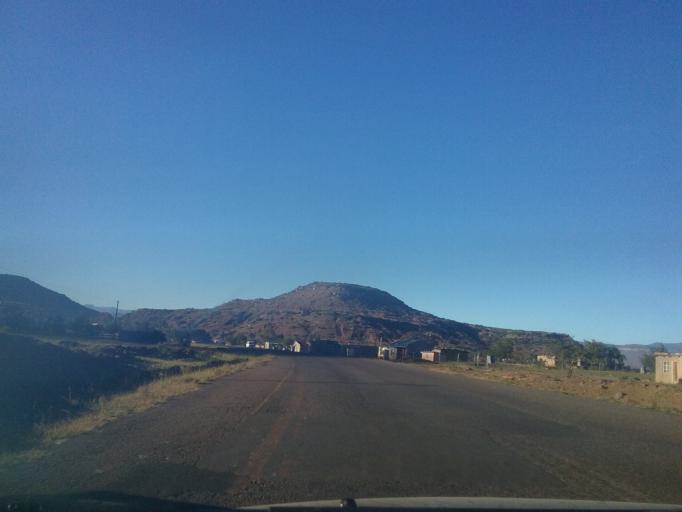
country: LS
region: Quthing
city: Quthing
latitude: -30.3339
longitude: 27.5336
